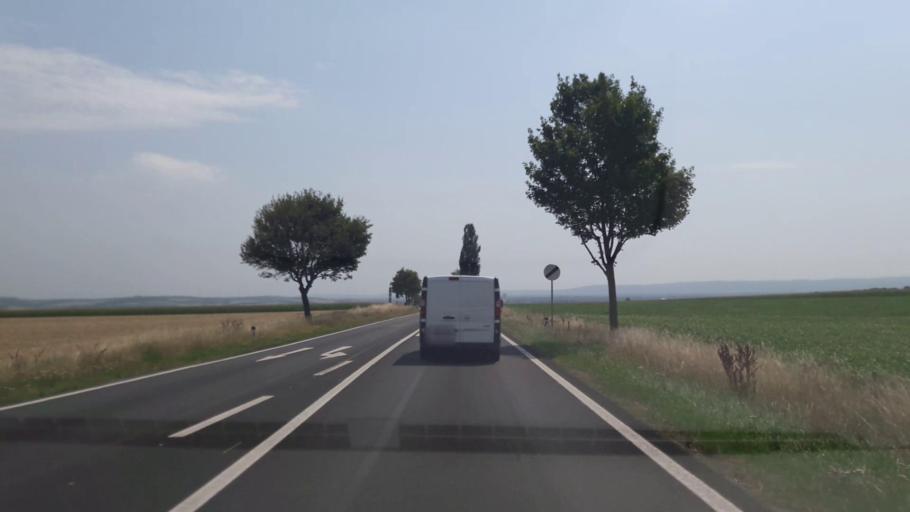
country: AT
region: Lower Austria
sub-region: Politischer Bezirk Wien-Umgebung
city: Rauchenwarth
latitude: 48.0897
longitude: 16.5536
